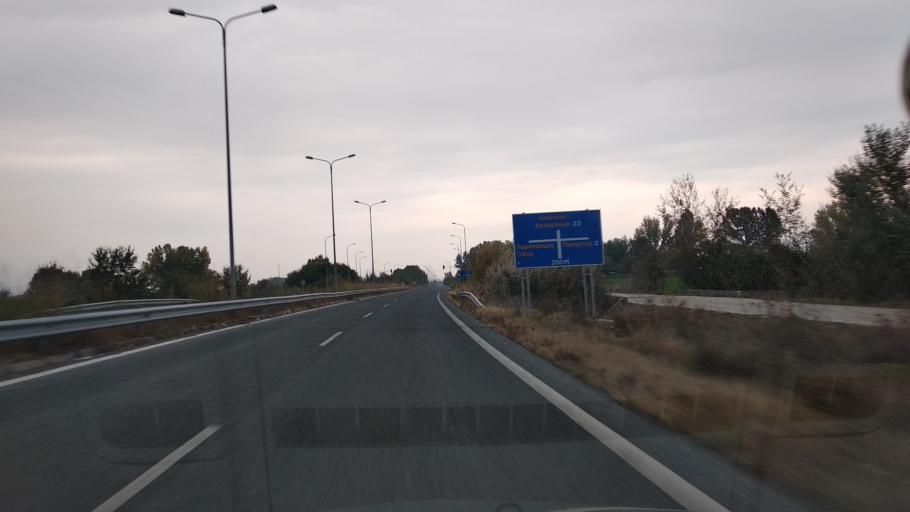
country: GR
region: Thessaly
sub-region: Trikala
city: Pyrgetos
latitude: 39.5388
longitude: 21.7360
